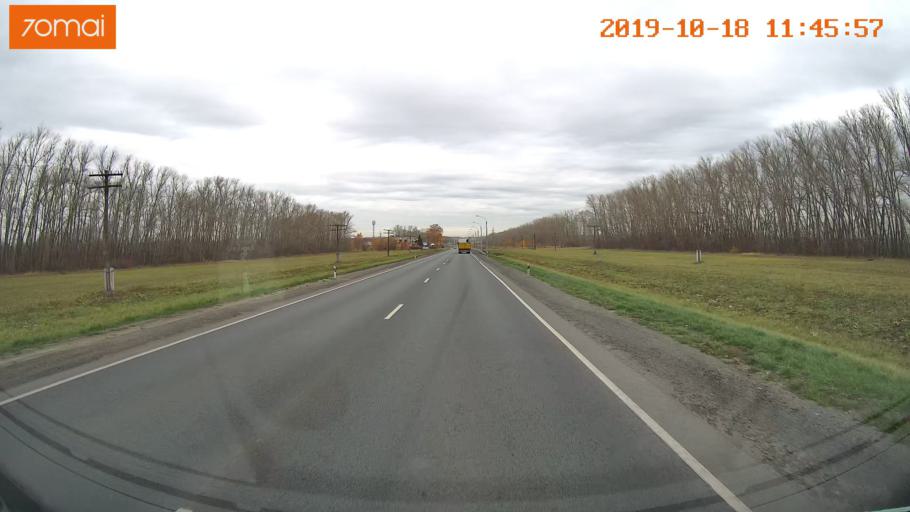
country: RU
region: Rjazan
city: Mikhaylov
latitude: 54.2152
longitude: 38.9771
